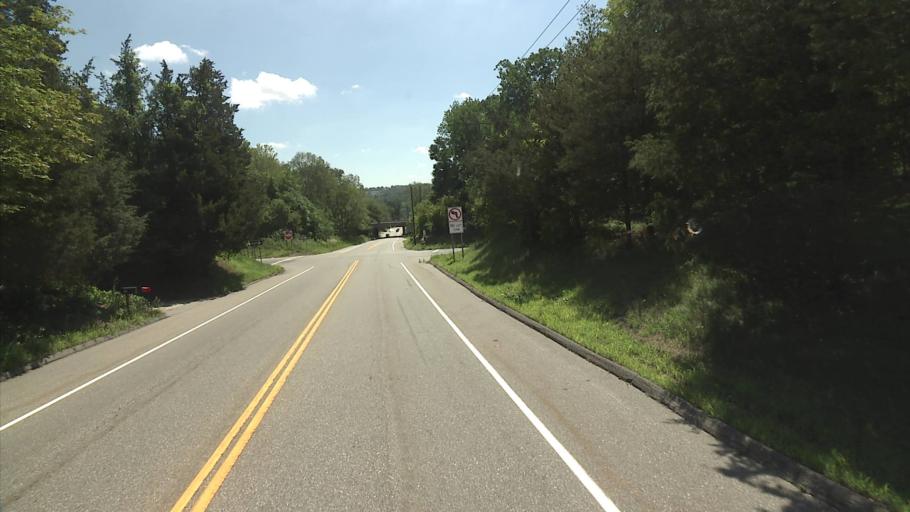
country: US
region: Connecticut
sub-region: Windham County
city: Plainfield
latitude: 41.6852
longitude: -71.9104
